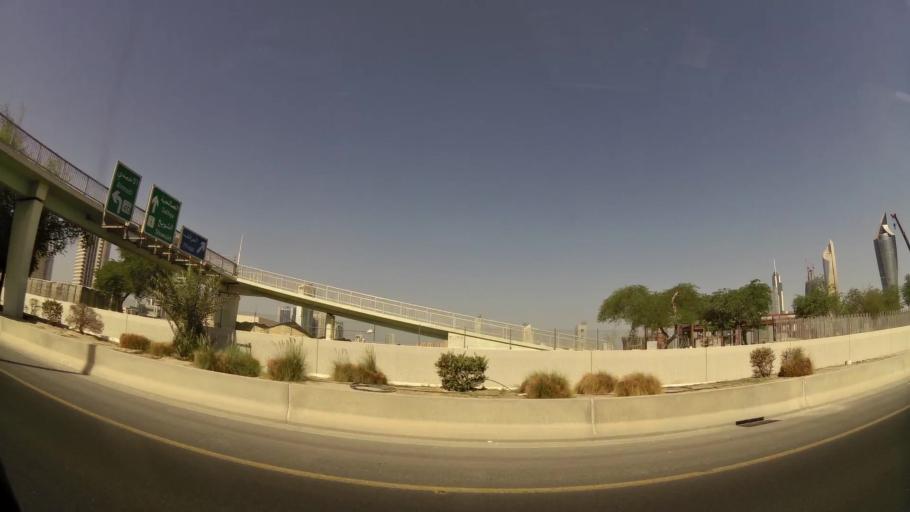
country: KW
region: Al Asimah
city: Ad Dasmah
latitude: 29.3625
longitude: 47.9890
